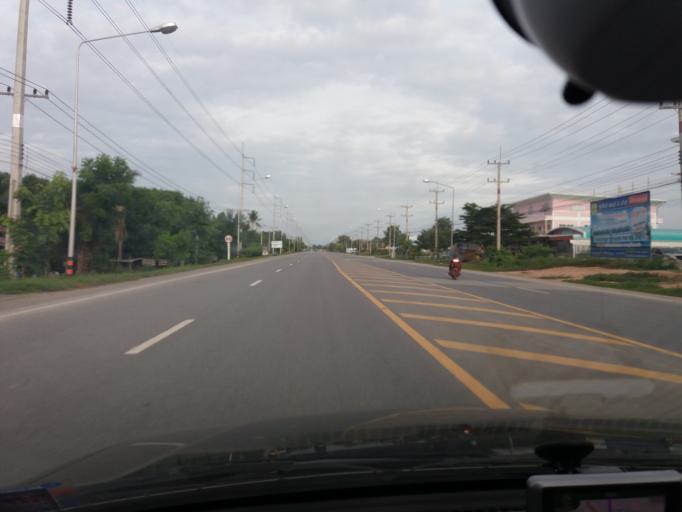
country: TH
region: Kanchanaburi
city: Huai Krachao
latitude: 14.3347
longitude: 99.7822
